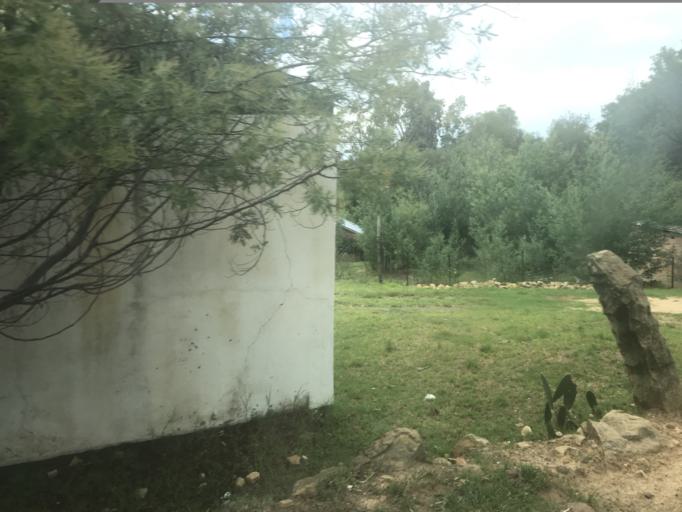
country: LS
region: Maseru
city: Nako
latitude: -29.6307
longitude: 27.5093
